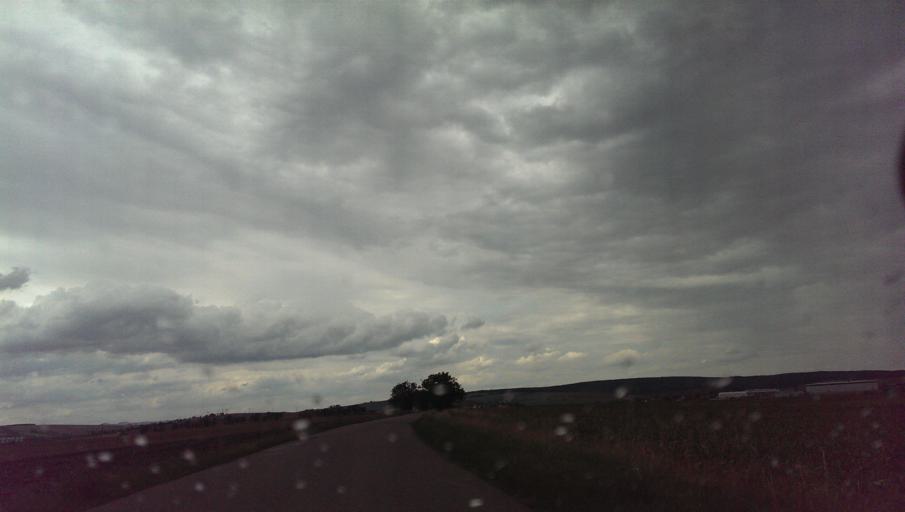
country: CZ
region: Zlin
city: Hluk
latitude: 48.9722
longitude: 17.5394
